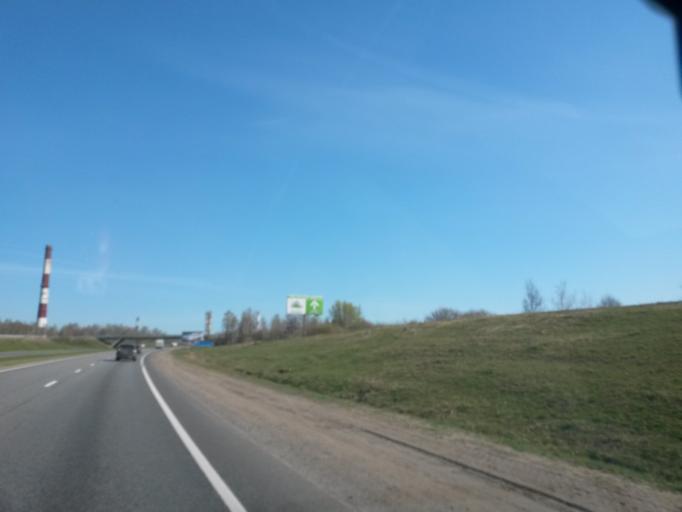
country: RU
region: Jaroslavl
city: Krasnyye Tkachi
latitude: 57.5260
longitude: 39.7840
